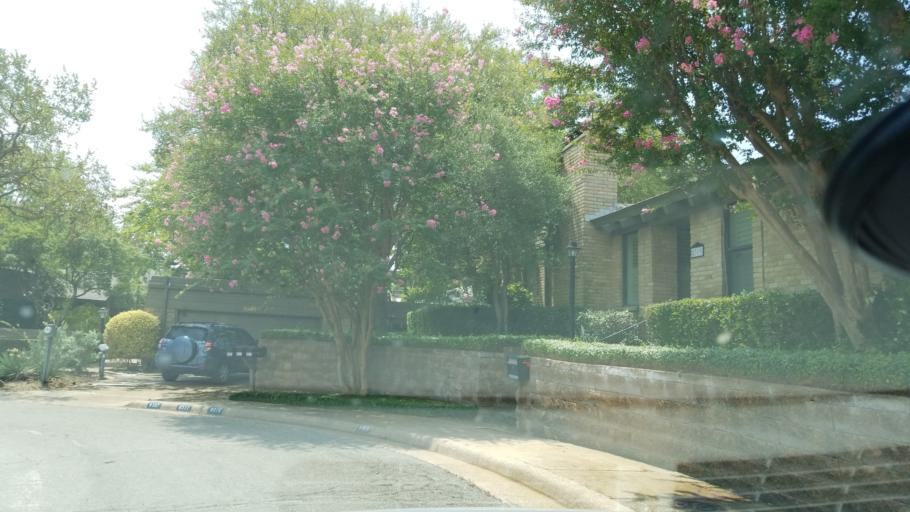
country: US
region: Texas
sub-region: Dallas County
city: Richardson
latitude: 32.8921
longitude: -96.7319
